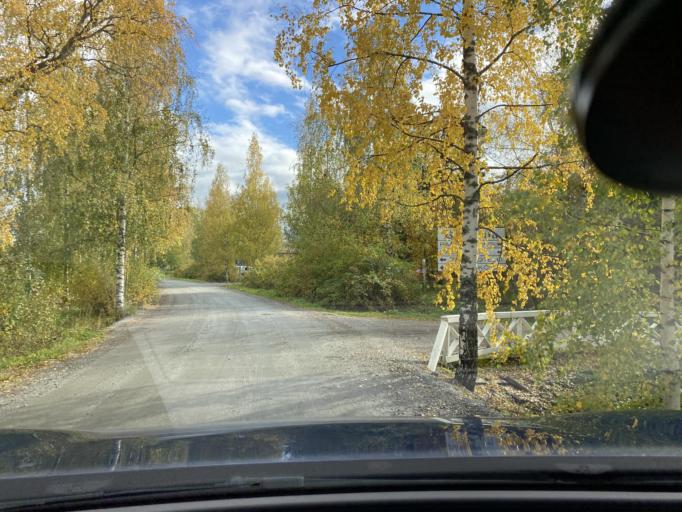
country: FI
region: Pirkanmaa
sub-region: Tampere
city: Nokia
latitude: 61.4710
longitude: 23.3554
